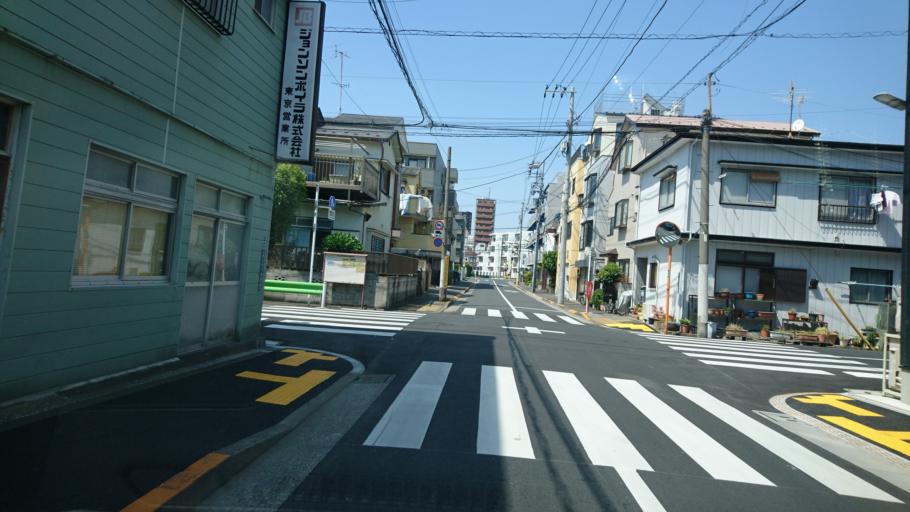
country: JP
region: Kanagawa
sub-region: Kawasaki-shi
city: Kawasaki
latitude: 35.5694
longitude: 139.7056
